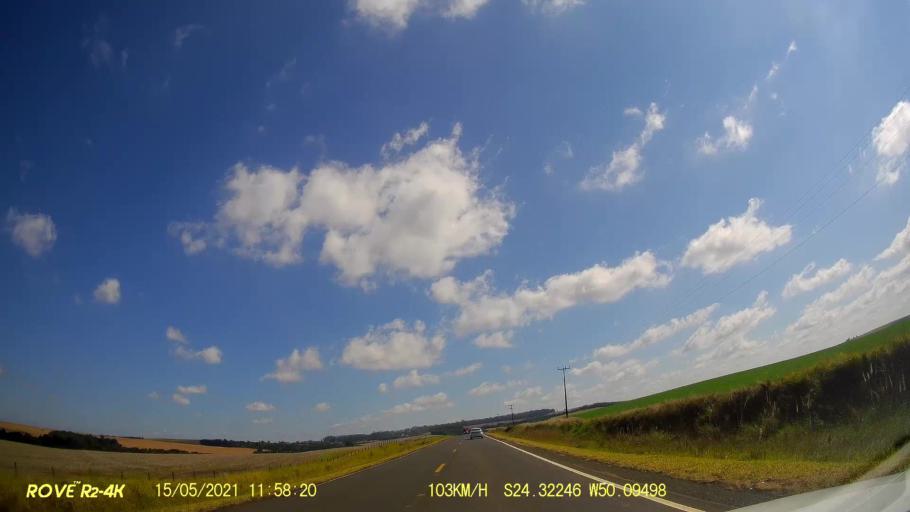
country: BR
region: Parana
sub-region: Pirai Do Sul
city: Pirai do Sul
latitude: -24.3222
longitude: -50.0953
